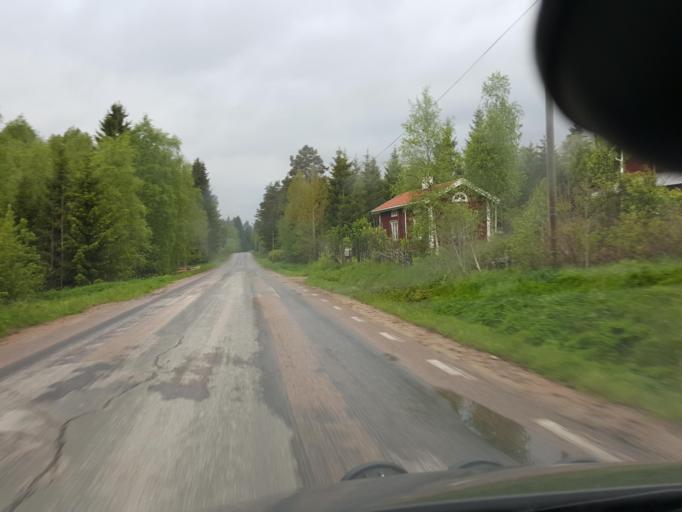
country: SE
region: Gaevleborg
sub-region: Ljusdals Kommun
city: Ljusdal
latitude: 61.8154
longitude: 16.1477
